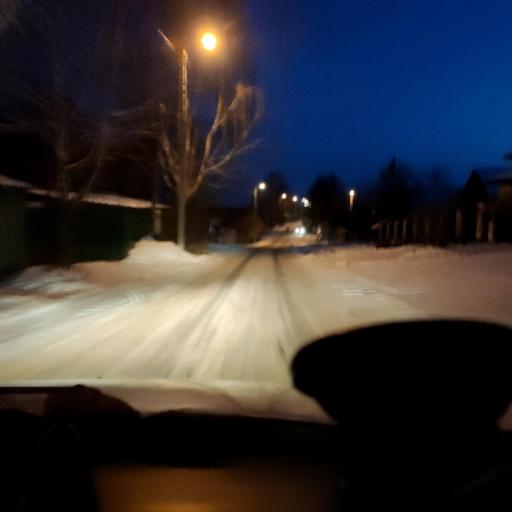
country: RU
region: Perm
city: Froly
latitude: 57.9493
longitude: 56.3021
